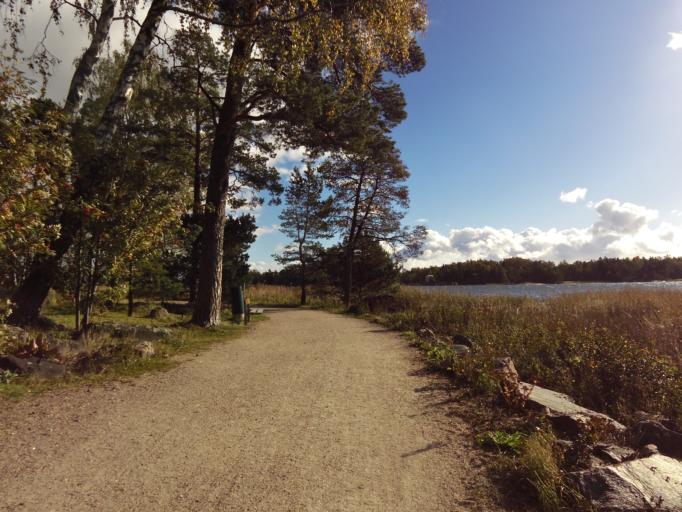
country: FI
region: Uusimaa
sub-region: Helsinki
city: Koukkuniemi
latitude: 60.1441
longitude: 24.7492
